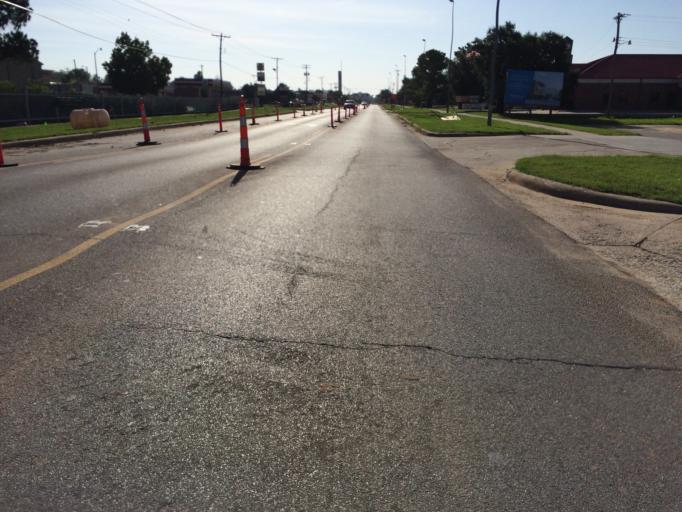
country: US
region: Oklahoma
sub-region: Cleveland County
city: Norman
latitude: 35.2039
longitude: -97.4720
